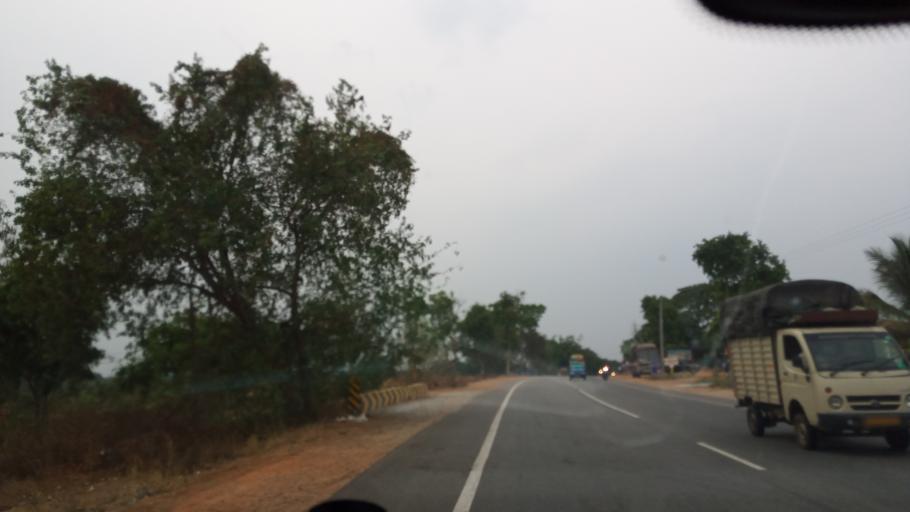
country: IN
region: Karnataka
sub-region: Mandya
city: Nagamangala
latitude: 12.7960
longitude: 76.7511
